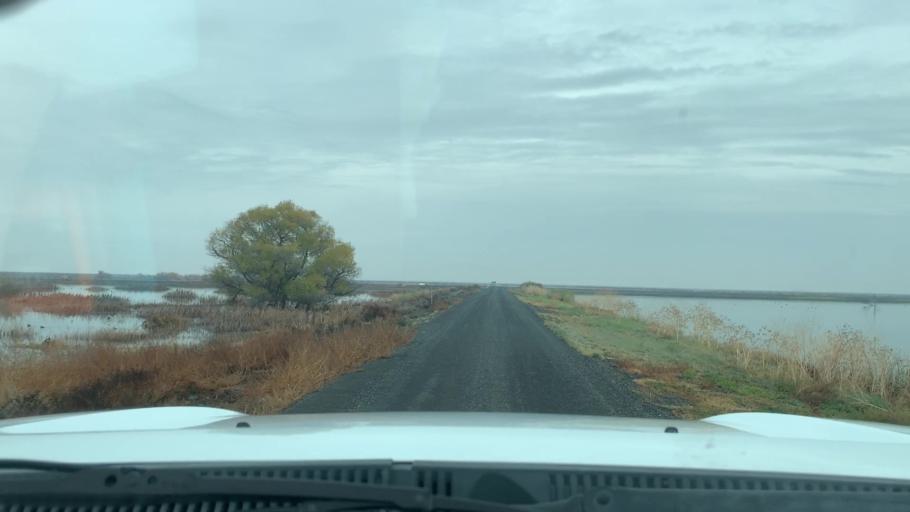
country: US
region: California
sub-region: Tulare County
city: Alpaugh
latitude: 35.7484
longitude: -119.5825
